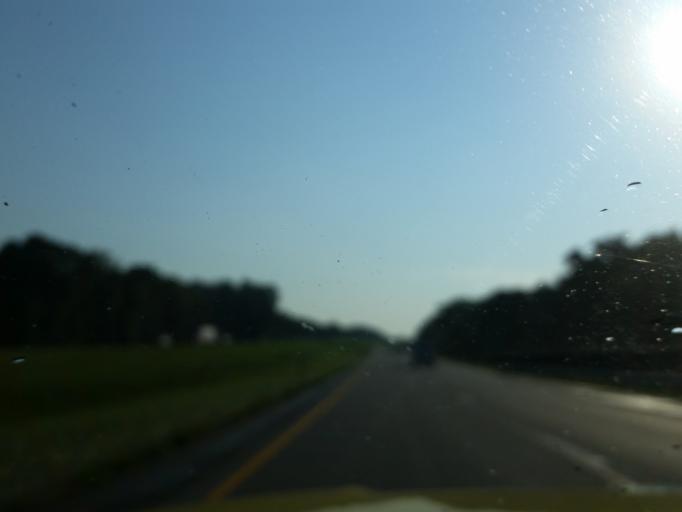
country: US
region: Pennsylvania
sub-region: York County
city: Hallam
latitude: 40.0195
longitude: -76.5789
